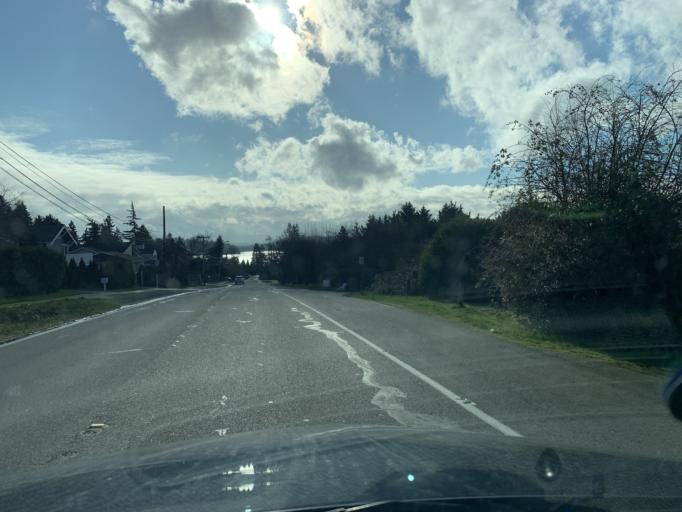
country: US
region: Washington
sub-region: King County
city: Mercer Island
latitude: 47.5856
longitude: -122.2486
